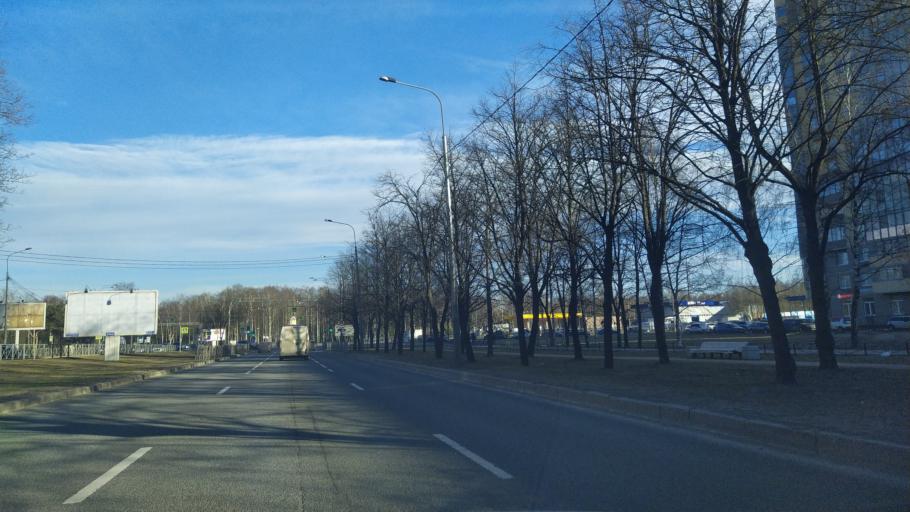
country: RU
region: Leningrad
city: Kalininskiy
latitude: 59.9949
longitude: 30.3887
